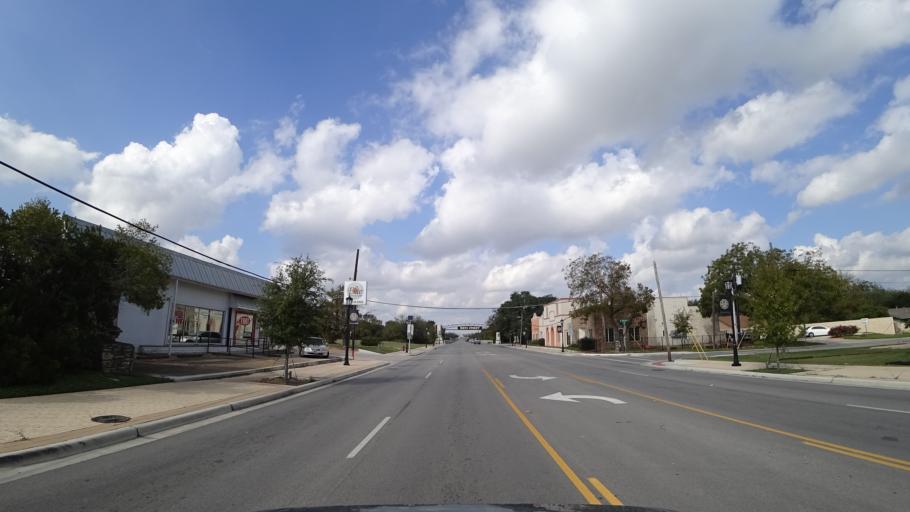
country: US
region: Texas
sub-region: Williamson County
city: Round Rock
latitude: 30.5116
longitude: -97.6800
